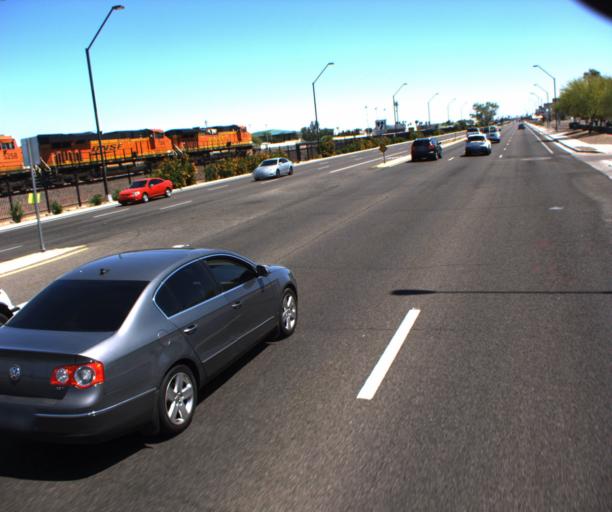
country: US
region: Arizona
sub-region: Maricopa County
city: Peoria
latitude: 33.5881
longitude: -112.2457
